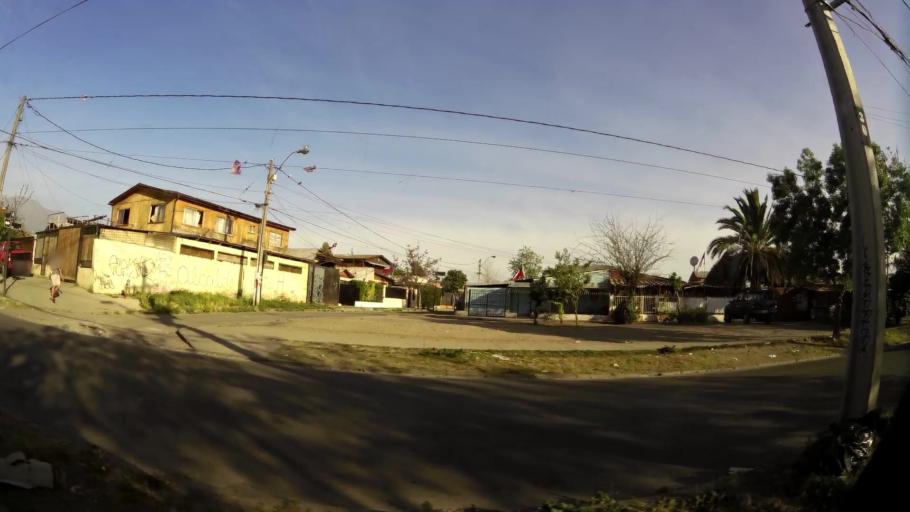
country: CL
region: Santiago Metropolitan
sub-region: Provincia de Santiago
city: Santiago
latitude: -33.5157
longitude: -70.6229
